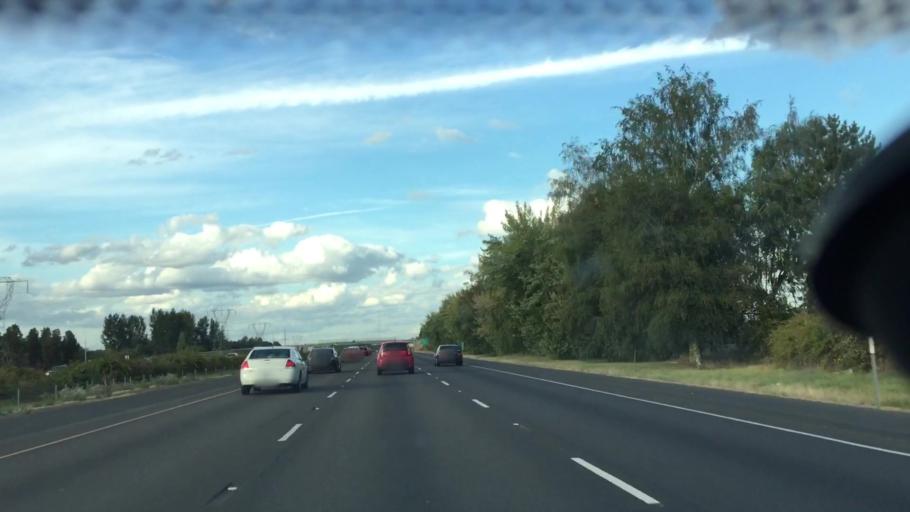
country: US
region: Oregon
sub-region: Marion County
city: Woodburn
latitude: 45.1647
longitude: -122.8687
